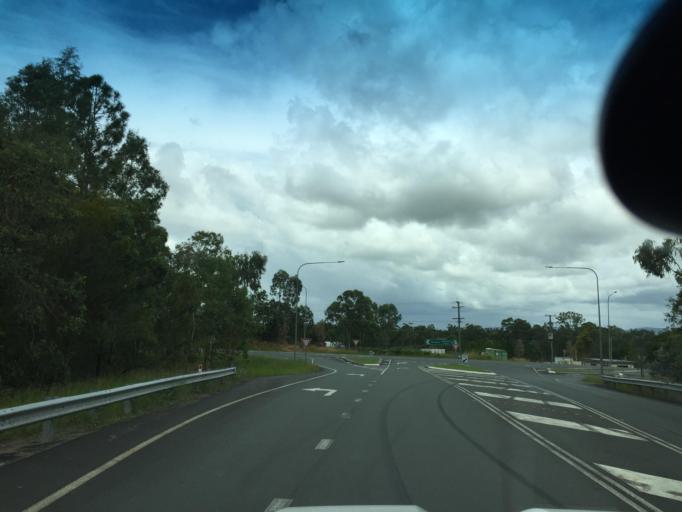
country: AU
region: Queensland
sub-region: Moreton Bay
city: Caboolture
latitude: -27.0617
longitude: 152.9080
